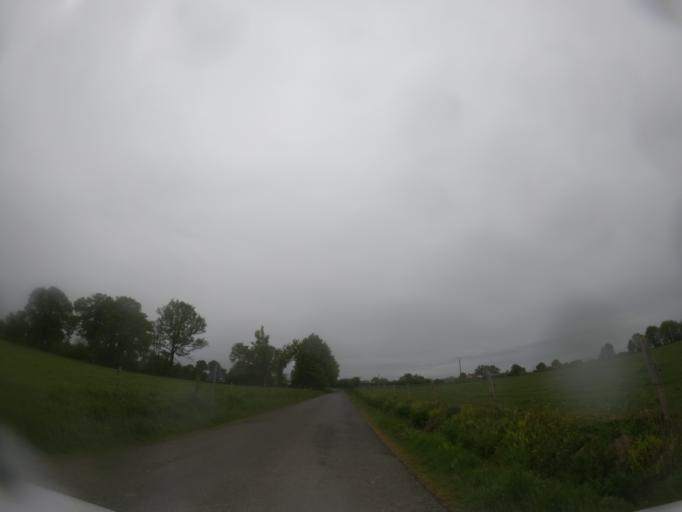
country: FR
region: Brittany
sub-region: Departement d'Ille-et-Vilaine
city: La Guerche-de-Bretagne
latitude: 47.9507
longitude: -1.1331
